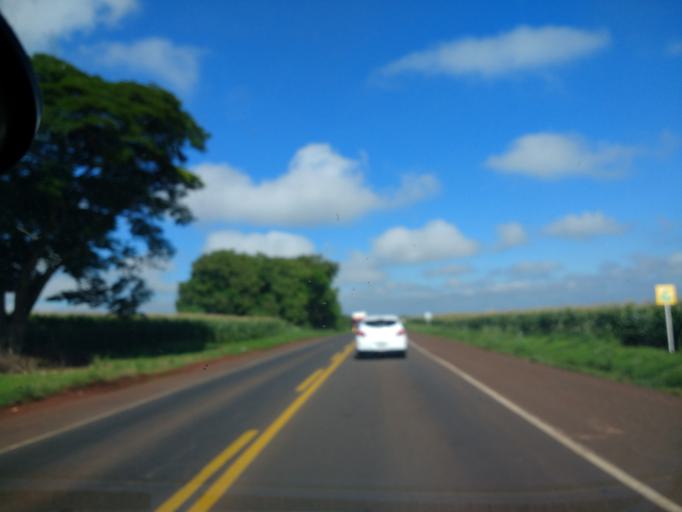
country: BR
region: Parana
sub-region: Paicandu
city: Paicandu
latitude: -23.5380
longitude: -52.2210
